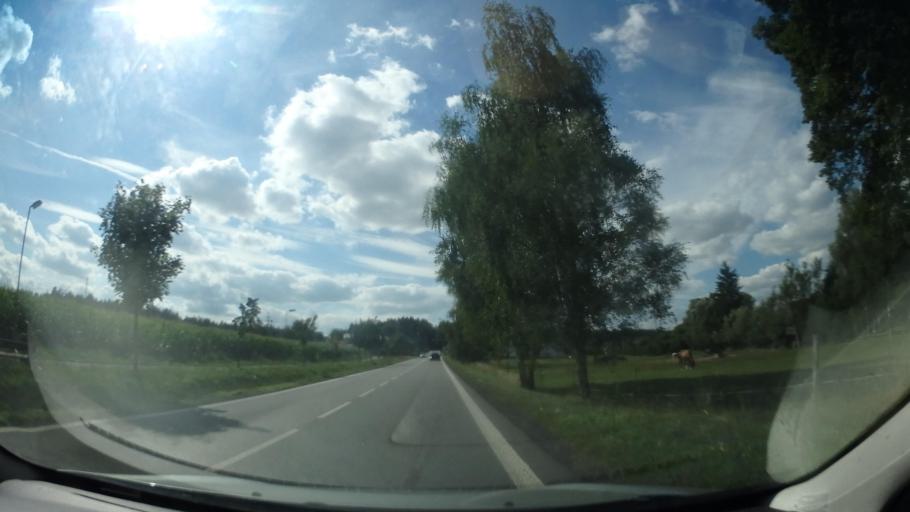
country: CZ
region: Vysocina
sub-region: Okres Zd'ar nad Sazavou
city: Zd'ar nad Sazavou
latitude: 49.5622
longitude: 15.9052
